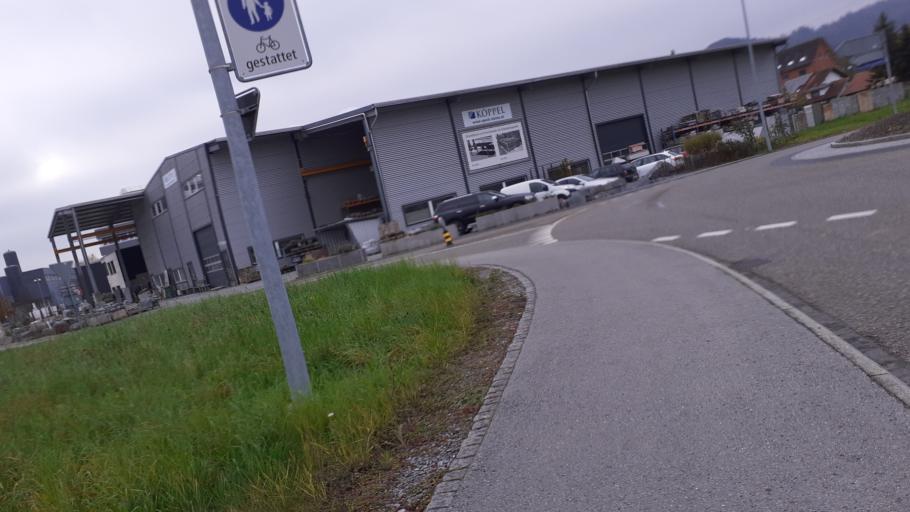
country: CH
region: Saint Gallen
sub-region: Wahlkreis Rheintal
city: Au
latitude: 47.4209
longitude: 9.6374
